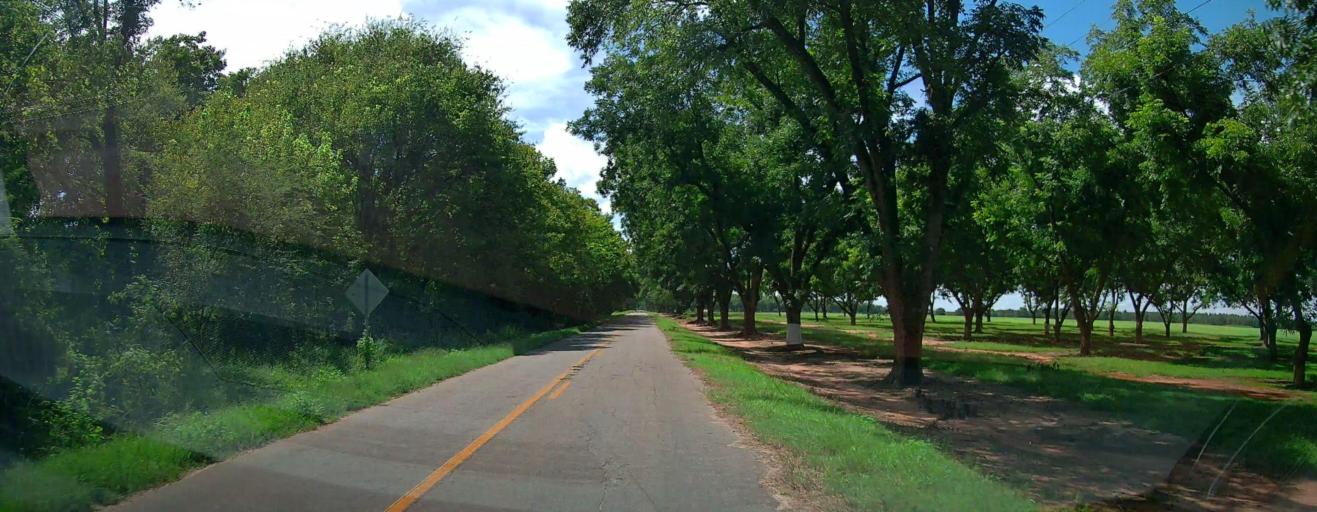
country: US
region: Georgia
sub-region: Macon County
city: Marshallville
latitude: 32.4485
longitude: -83.9825
